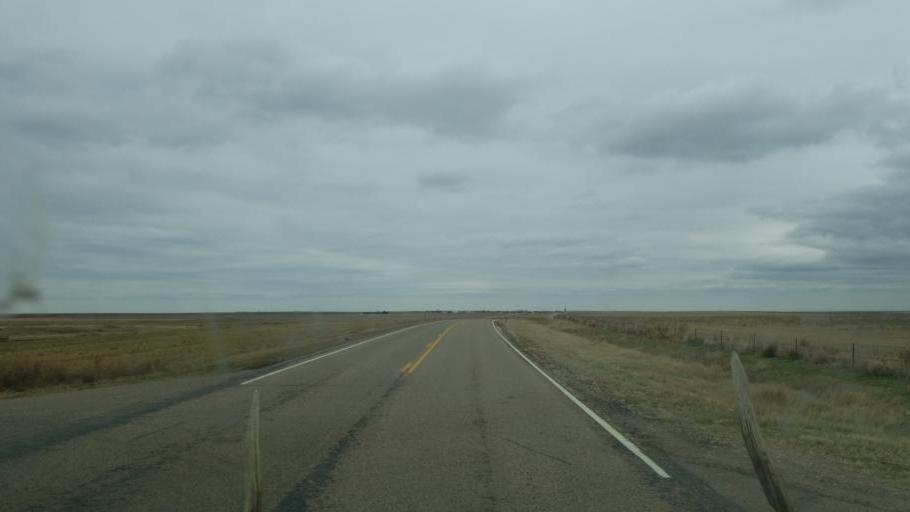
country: US
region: Colorado
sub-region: Cheyenne County
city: Cheyenne Wells
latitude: 38.8532
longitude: -102.2214
